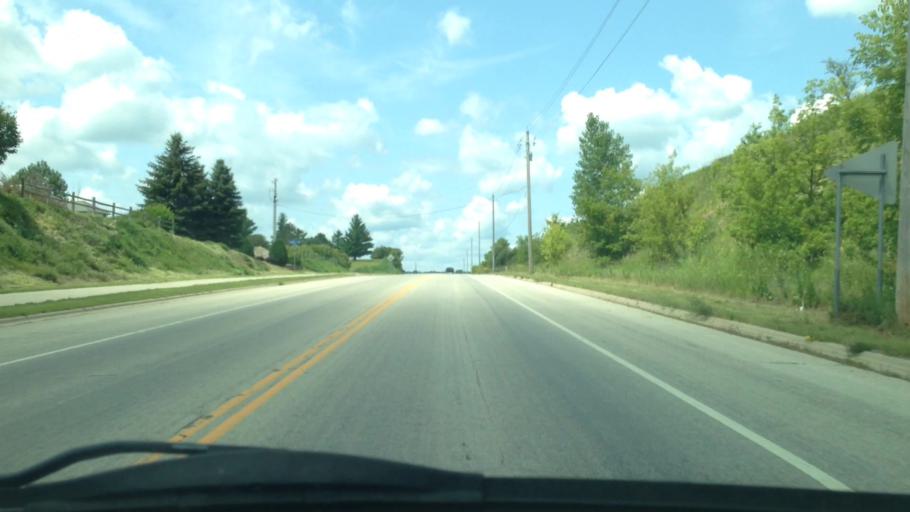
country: US
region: Minnesota
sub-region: Olmsted County
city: Rochester
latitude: 43.9531
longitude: -92.4832
